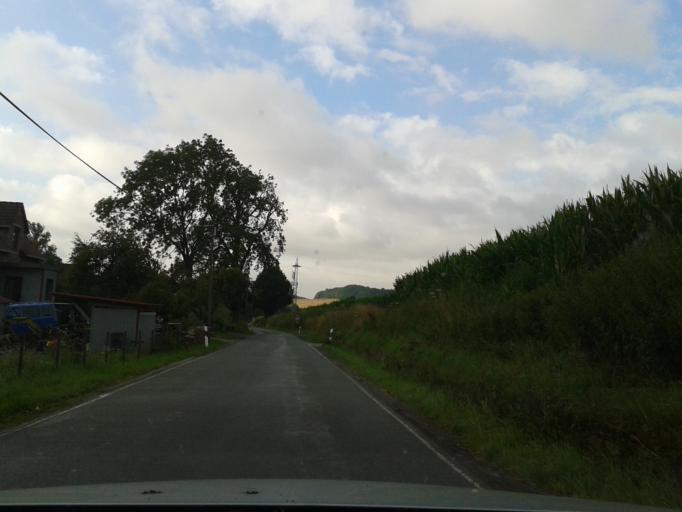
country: DE
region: North Rhine-Westphalia
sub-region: Regierungsbezirk Detmold
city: Dorentrup
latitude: 51.9934
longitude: 8.9936
